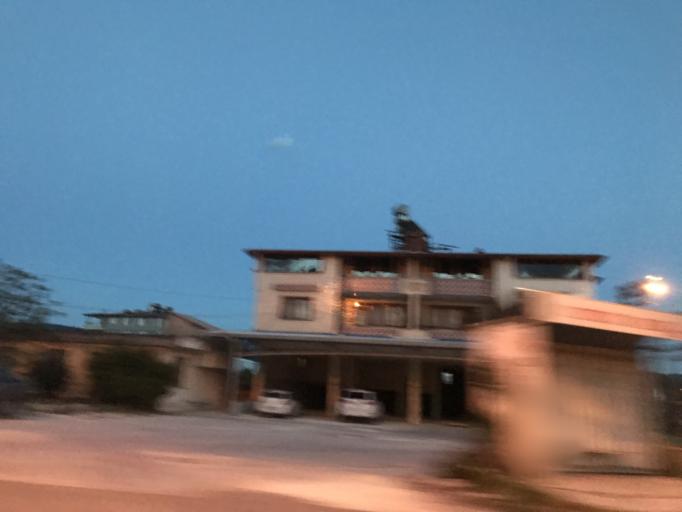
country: TR
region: Hatay
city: Asagiokcular
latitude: 36.1860
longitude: 36.1222
